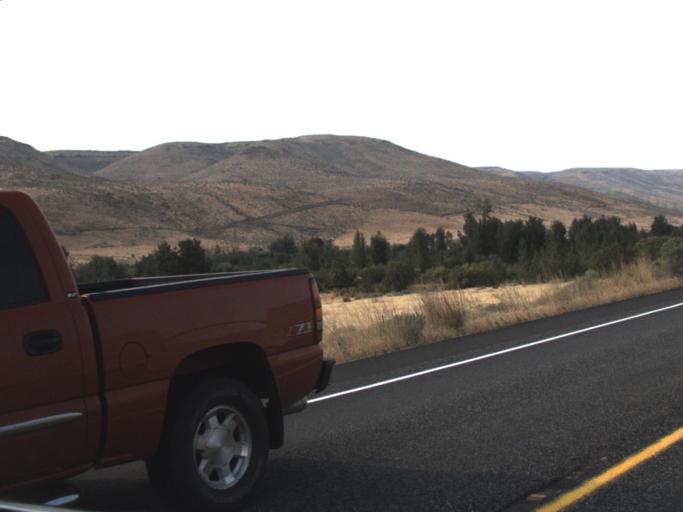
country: US
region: Washington
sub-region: Yakima County
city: Toppenish
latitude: 46.1805
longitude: -120.4986
